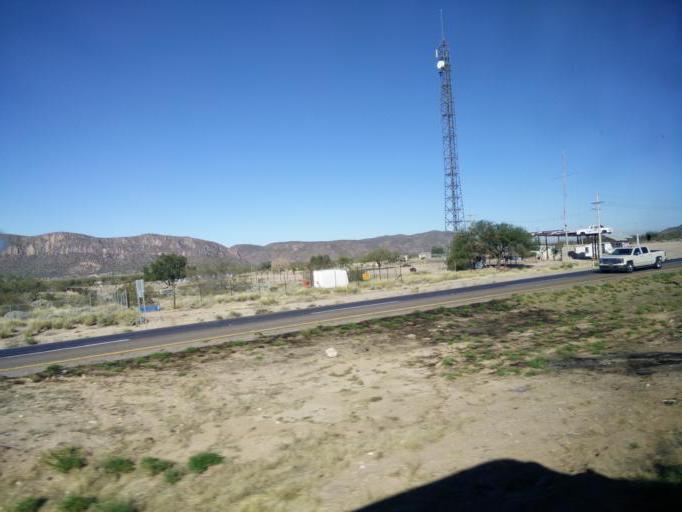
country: MX
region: Sonora
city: Hermosillo
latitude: 28.9590
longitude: -110.9629
